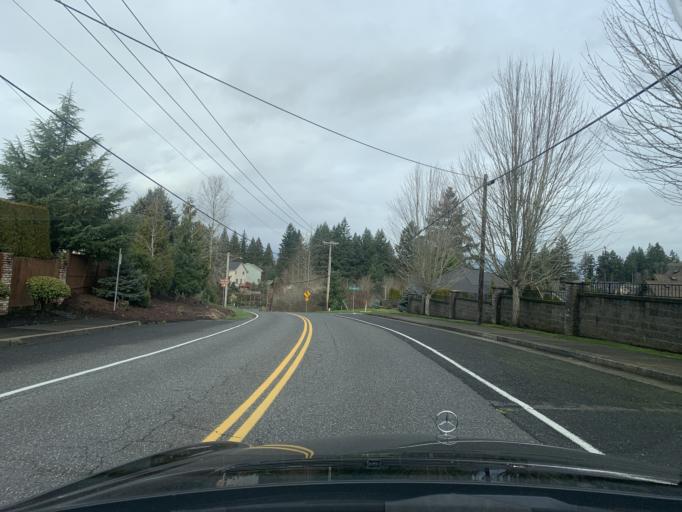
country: US
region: Oregon
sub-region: Multnomah County
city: Gresham
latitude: 45.4716
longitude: -122.4316
